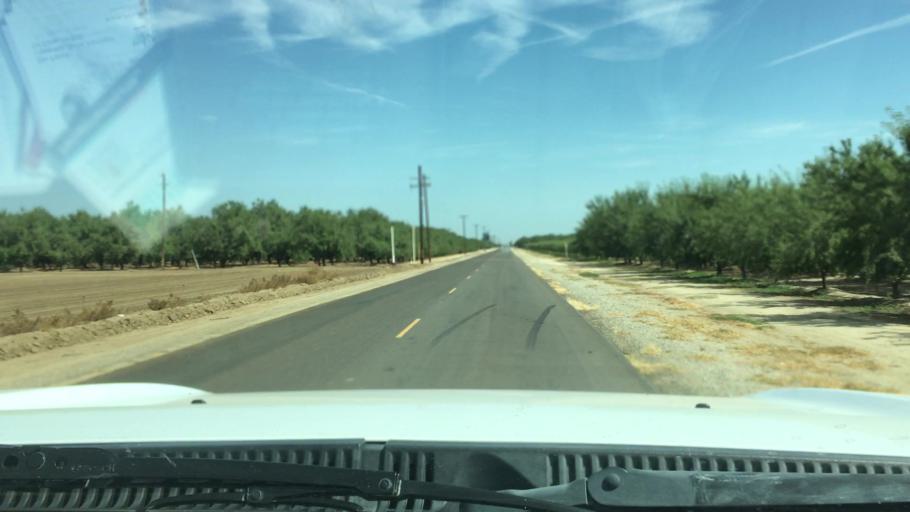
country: US
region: California
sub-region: Kern County
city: Wasco
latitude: 35.5209
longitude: -119.3499
